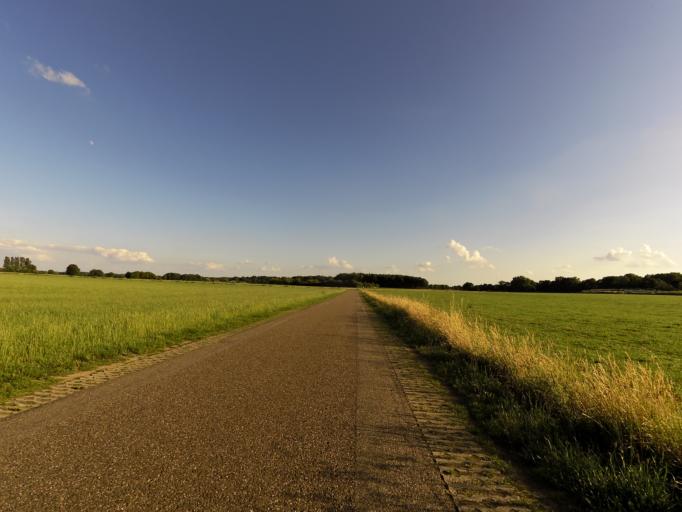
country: NL
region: Gelderland
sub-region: Oude IJsselstreek
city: Gendringen
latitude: 51.8875
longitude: 6.3939
